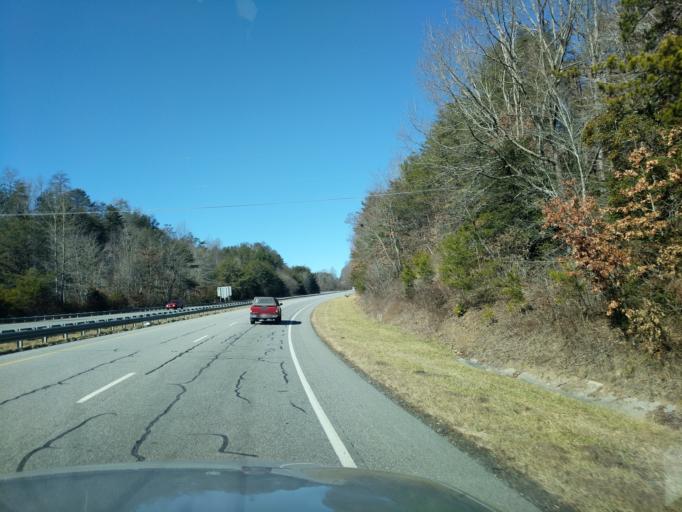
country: US
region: North Carolina
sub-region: Swain County
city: Cherokee
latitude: 35.4320
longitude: -83.3638
